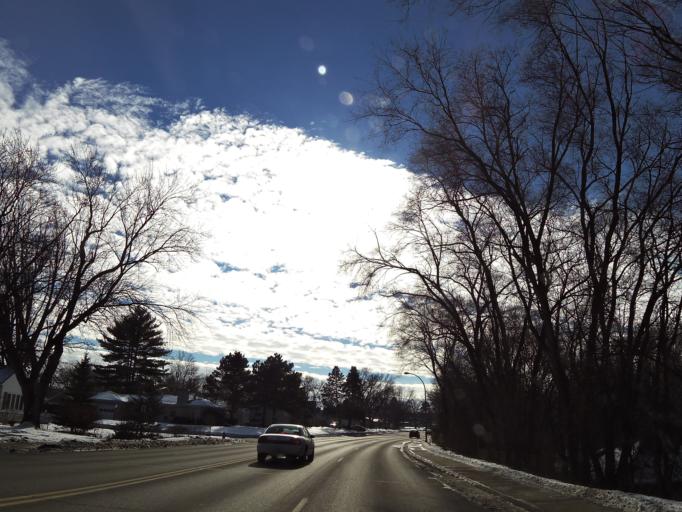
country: US
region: Minnesota
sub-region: Hennepin County
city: Richfield
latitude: 44.8804
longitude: -93.2879
